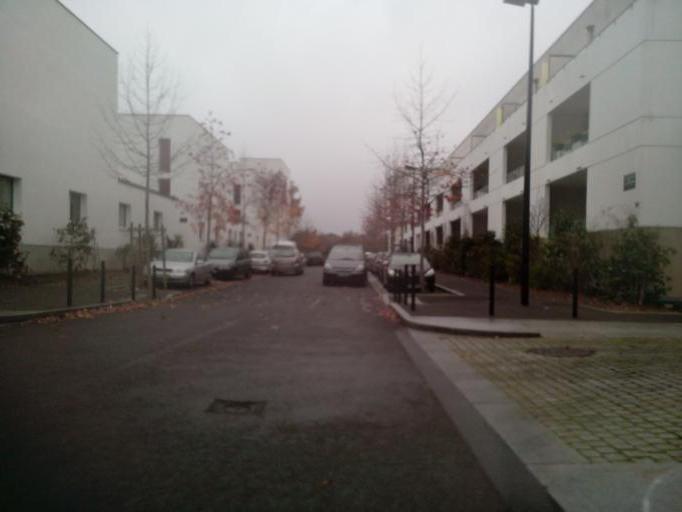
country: FR
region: Brittany
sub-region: Departement d'Ille-et-Vilaine
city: Saint-Jacques-de-la-Lande
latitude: 48.0796
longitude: -1.7176
